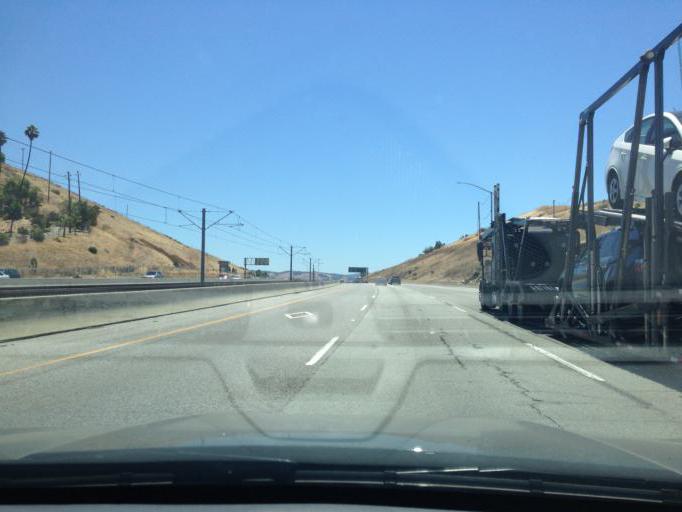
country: US
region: California
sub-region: Santa Clara County
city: Seven Trees
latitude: 37.2892
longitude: -121.8709
